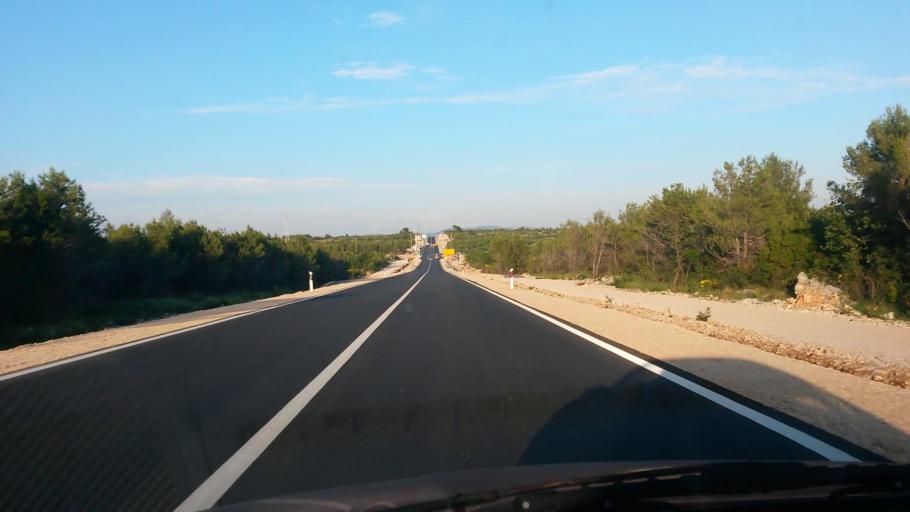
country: HR
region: Sibensko-Kniniska
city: Vodice
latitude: 43.7757
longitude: 15.7682
